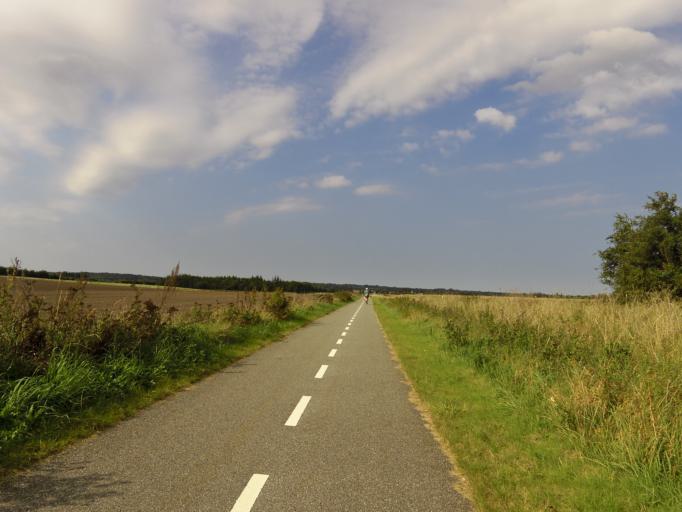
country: DK
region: South Denmark
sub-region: Vejen Kommune
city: Vejen
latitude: 55.4326
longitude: 9.1431
